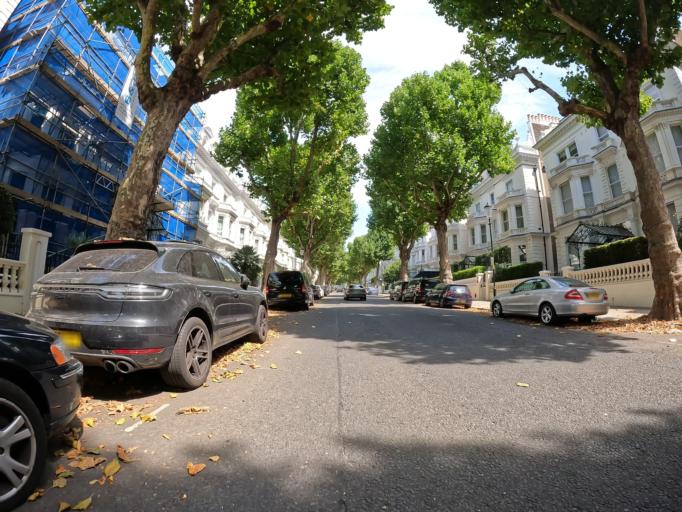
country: GB
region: England
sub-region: Greater London
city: Kensington
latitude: 51.5048
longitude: -0.2078
